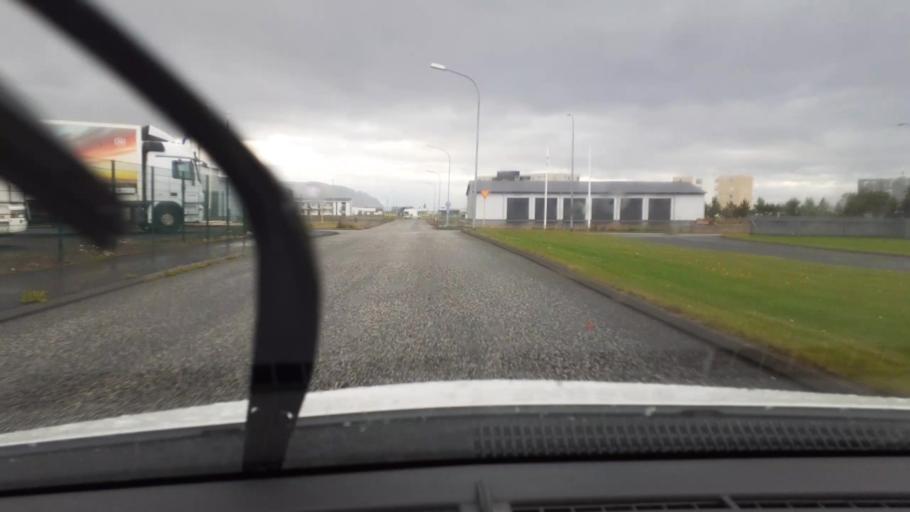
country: IS
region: West
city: Akranes
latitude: 64.3262
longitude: -22.0604
